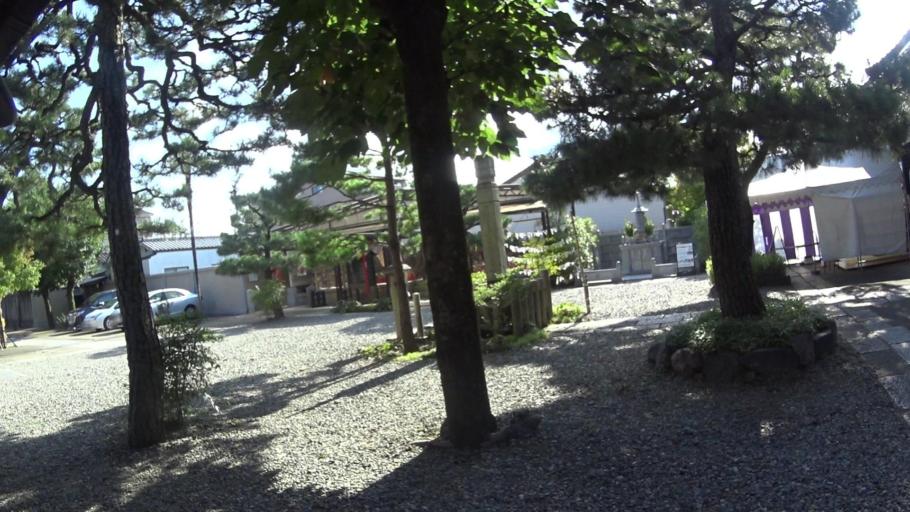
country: RU
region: Rostov
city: Remontnoye
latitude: 46.5006
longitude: 43.7645
